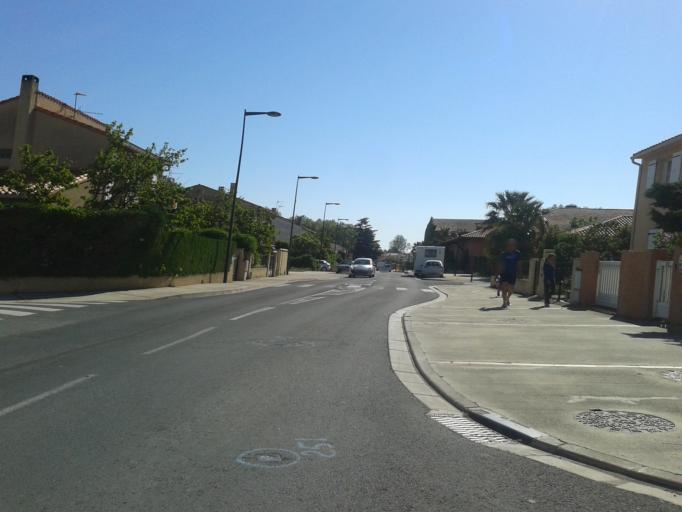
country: FR
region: Languedoc-Roussillon
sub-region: Departement des Pyrenees-Orientales
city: Toulouges
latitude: 42.6727
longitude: 2.8297
